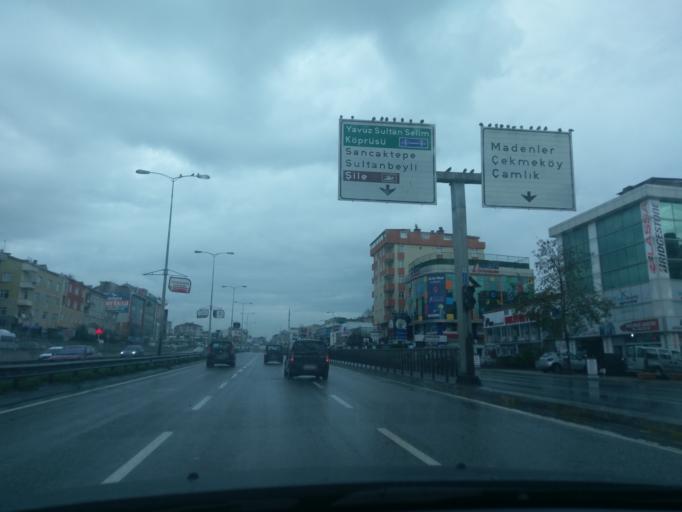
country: TR
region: Istanbul
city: Samandira
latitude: 41.0145
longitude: 29.1854
